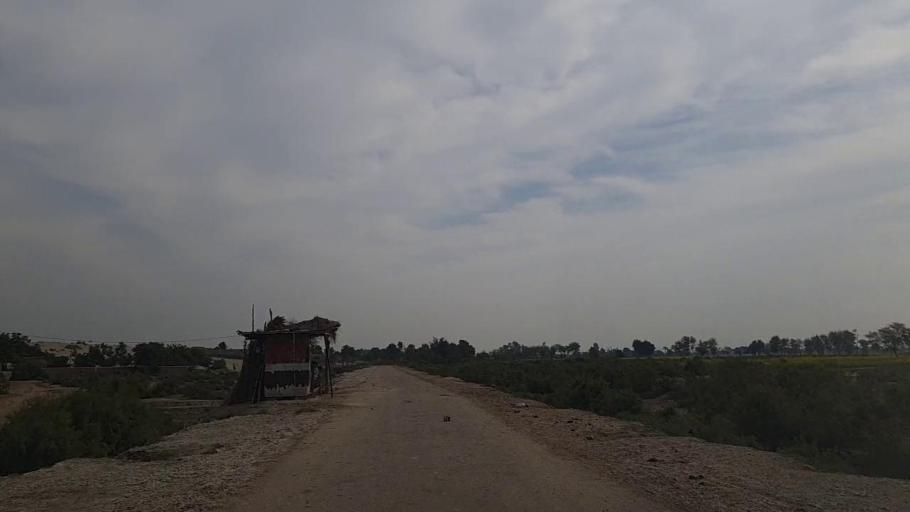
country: PK
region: Sindh
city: Daur
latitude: 26.4294
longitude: 68.4714
